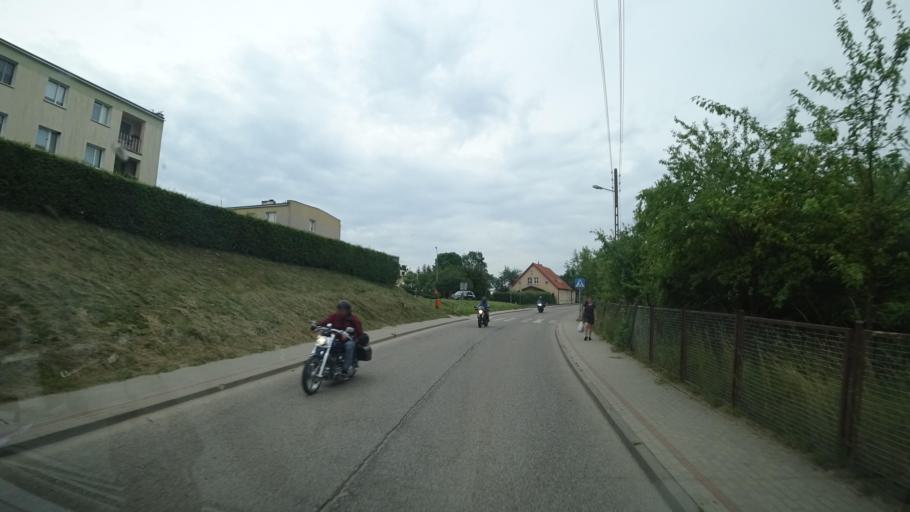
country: PL
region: Warmian-Masurian Voivodeship
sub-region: Powiat gizycki
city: Ryn
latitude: 53.9342
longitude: 21.5493
